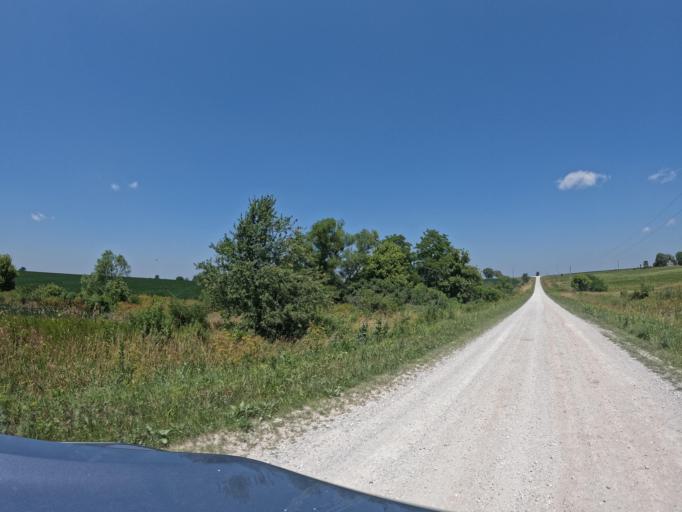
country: US
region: Iowa
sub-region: Keokuk County
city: Sigourney
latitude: 41.2714
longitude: -92.1701
